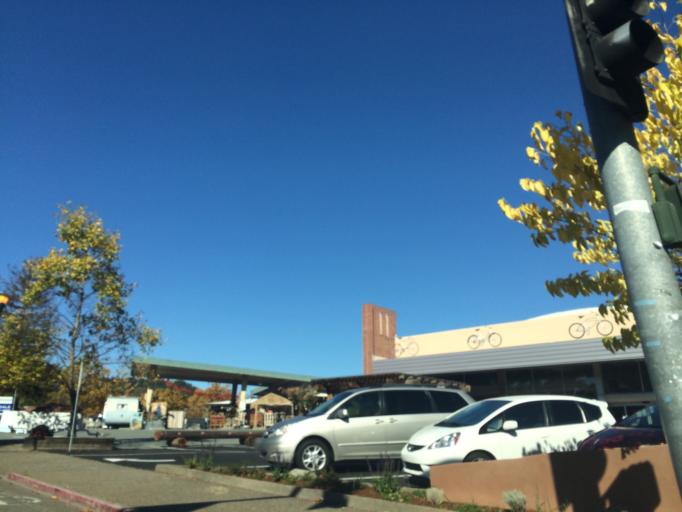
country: US
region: California
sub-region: Marin County
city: Fairfax
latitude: 37.9874
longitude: -122.5896
